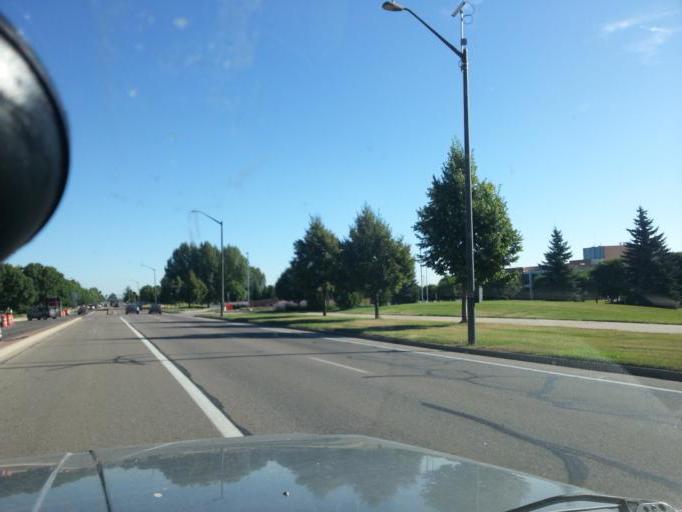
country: US
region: Colorado
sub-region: Larimer County
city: Fort Collins
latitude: 40.5404
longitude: -105.0393
